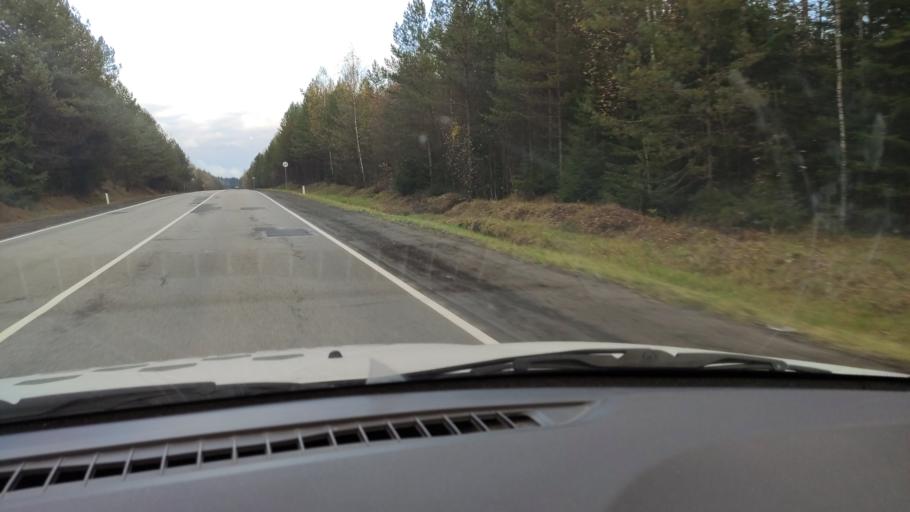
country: RU
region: Kirov
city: Belaya Kholunitsa
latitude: 58.8981
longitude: 50.9239
